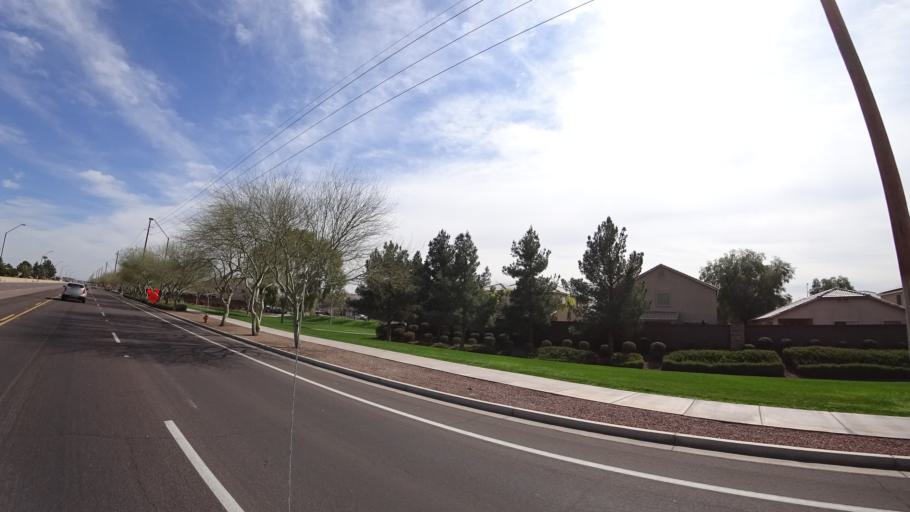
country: US
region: Arizona
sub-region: Maricopa County
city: Tolleson
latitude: 33.4789
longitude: -112.2880
